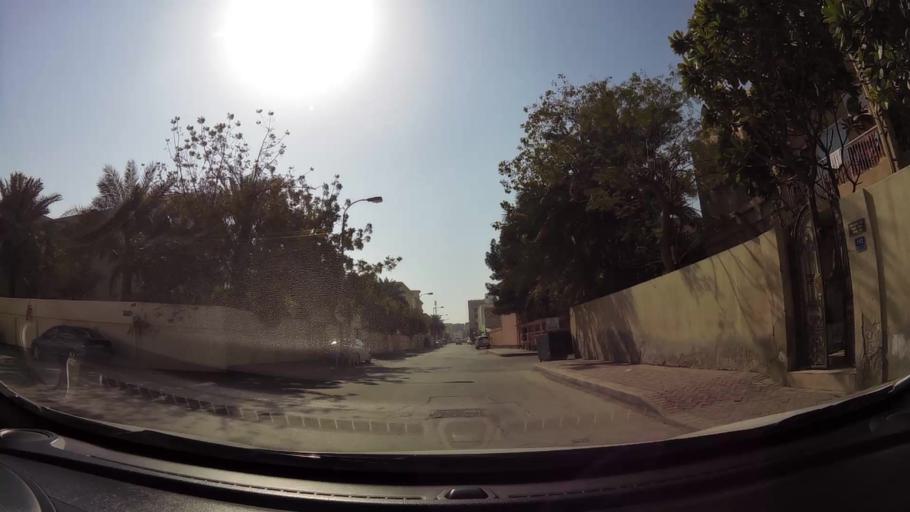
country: BH
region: Manama
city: Manama
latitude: 26.2116
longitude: 50.5891
